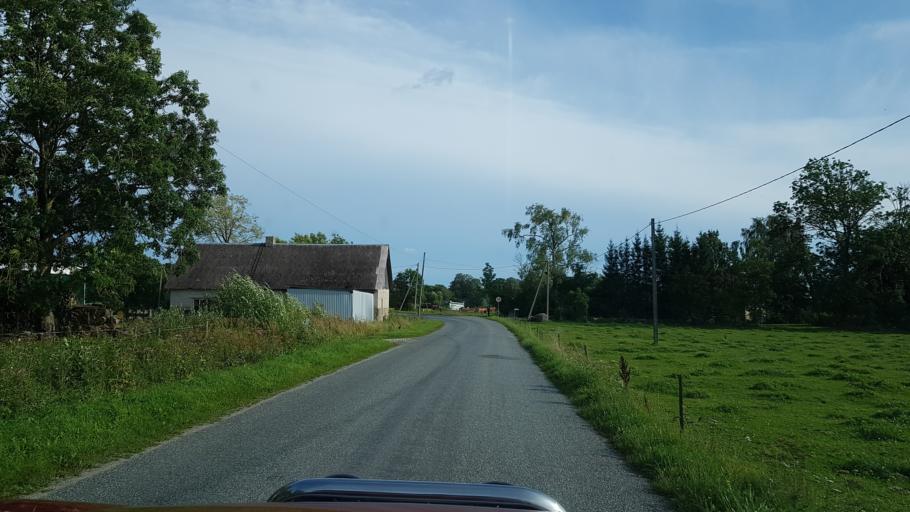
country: EE
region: Laeaene
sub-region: Lihula vald
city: Lihula
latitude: 58.4497
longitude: 23.9975
